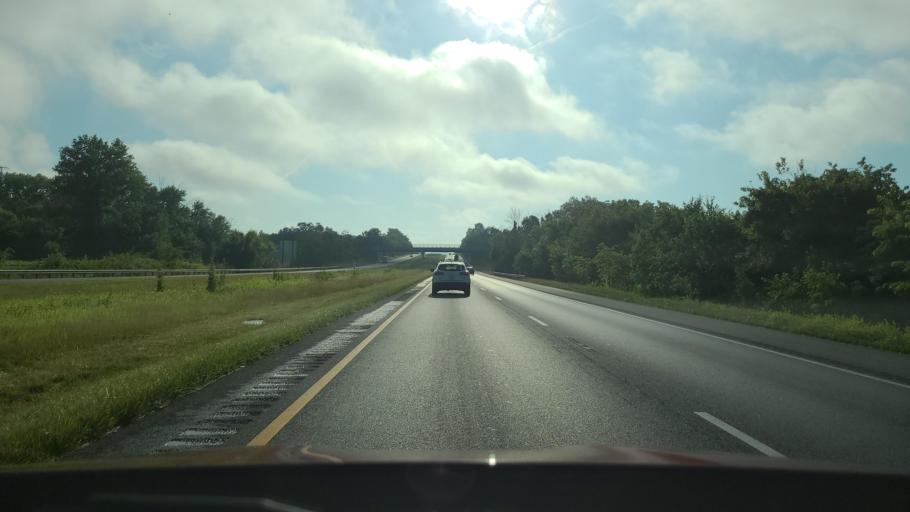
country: US
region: Maryland
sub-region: Frederick County
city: Brunswick
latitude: 39.3505
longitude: -77.6173
